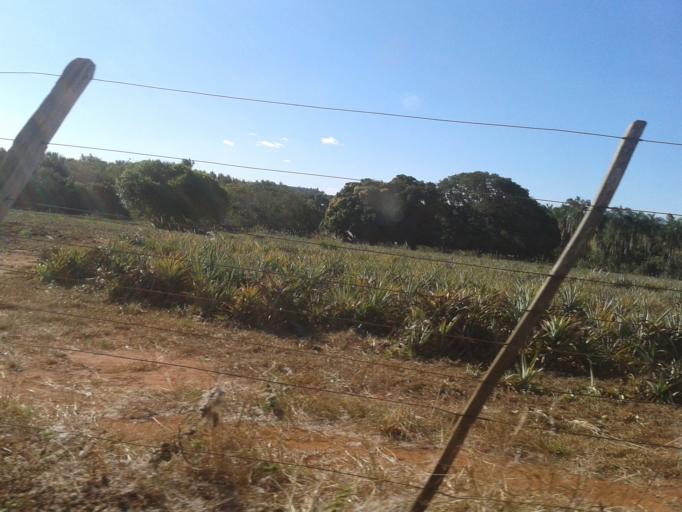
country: BR
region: Minas Gerais
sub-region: Centralina
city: Centralina
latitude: -18.7389
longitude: -49.1671
